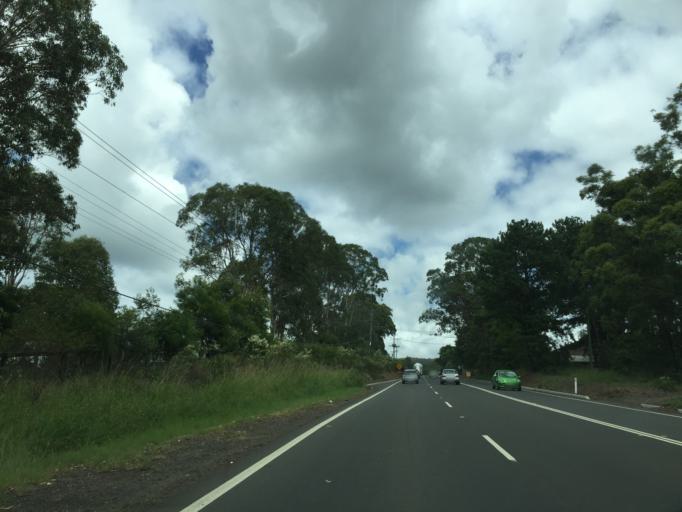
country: AU
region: New South Wales
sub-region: Hawkesbury
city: Richmond
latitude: -33.5473
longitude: 150.6575
